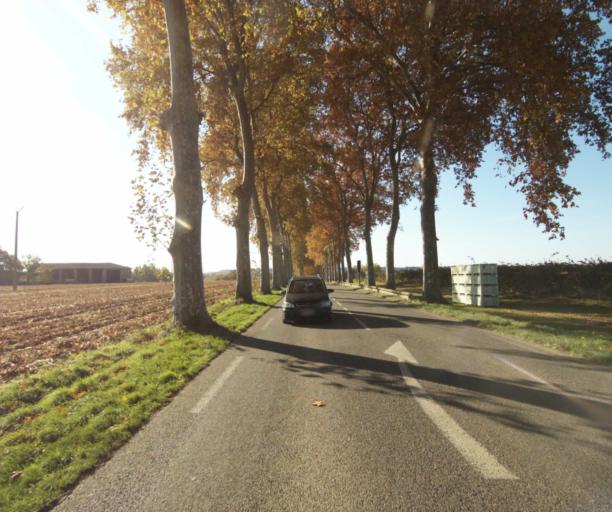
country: FR
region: Midi-Pyrenees
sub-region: Departement du Tarn-et-Garonne
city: Montech
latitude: 43.9546
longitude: 1.2067
